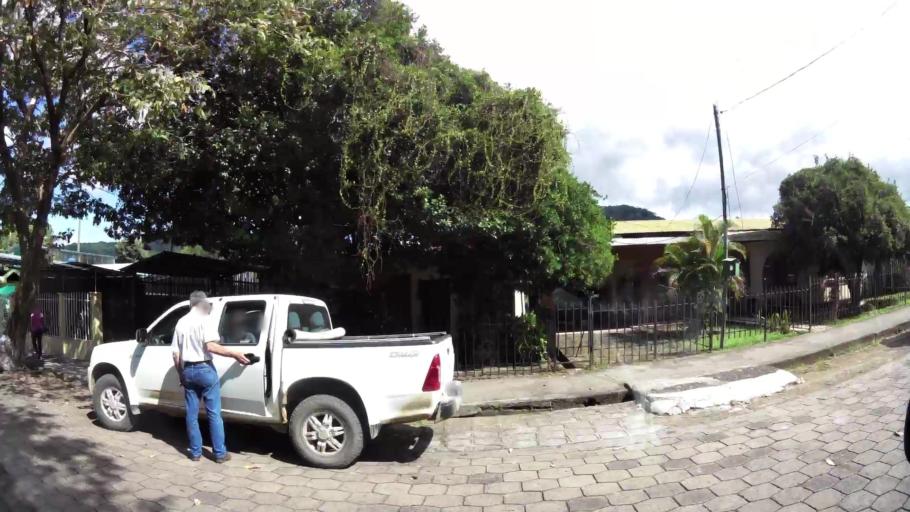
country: CR
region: Guanacaste
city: Juntas
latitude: 10.2807
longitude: -84.9588
